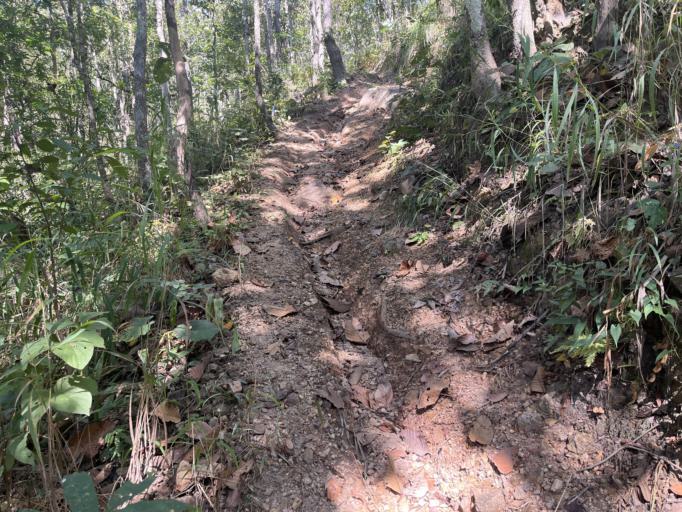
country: TH
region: Chiang Mai
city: San Sai
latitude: 18.9426
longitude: 99.0685
